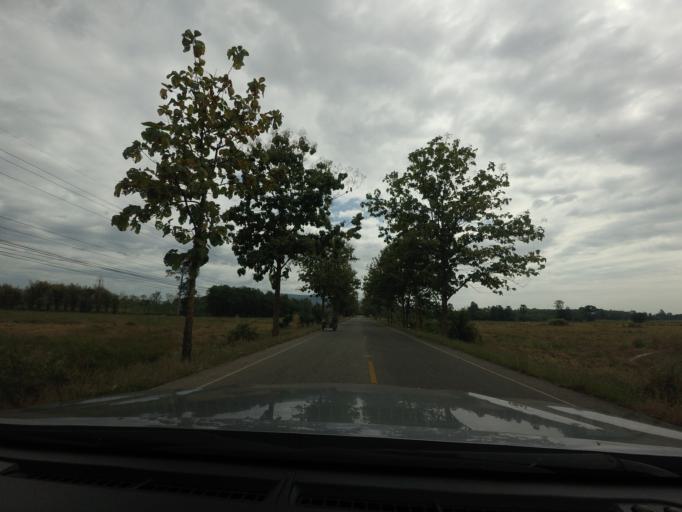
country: TH
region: Phitsanulok
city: Wang Thong
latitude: 16.6952
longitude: 100.5204
